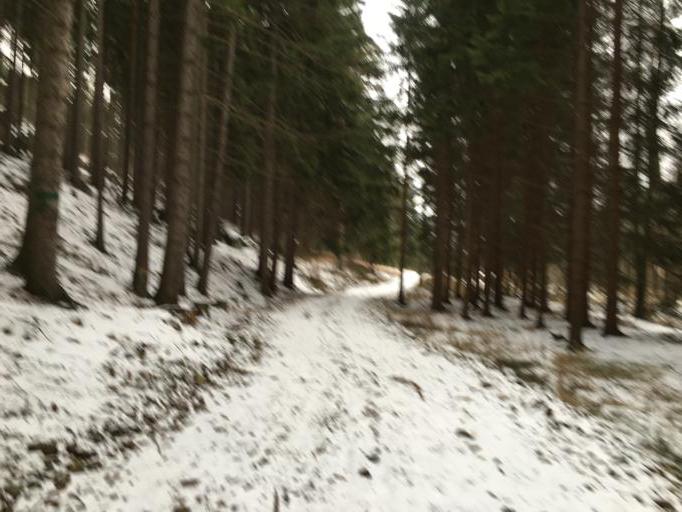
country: PL
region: Lower Silesian Voivodeship
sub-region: Powiat kamiennogorski
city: Krzeszow
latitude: 50.6951
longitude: 16.0988
